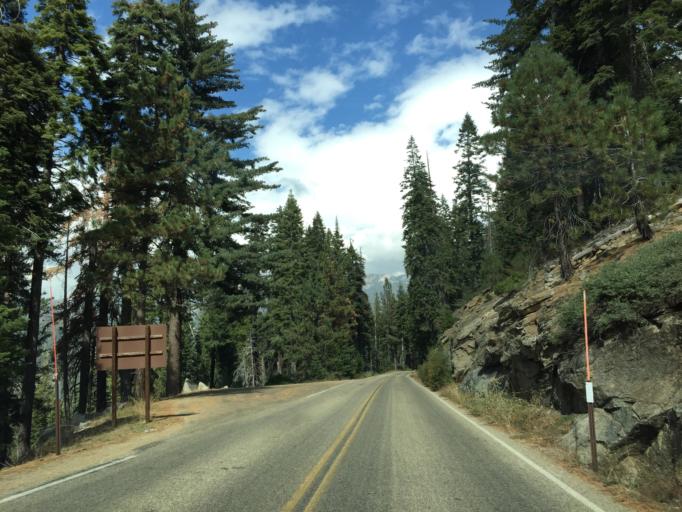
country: US
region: California
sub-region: Tulare County
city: Three Rivers
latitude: 36.5915
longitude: -118.7518
